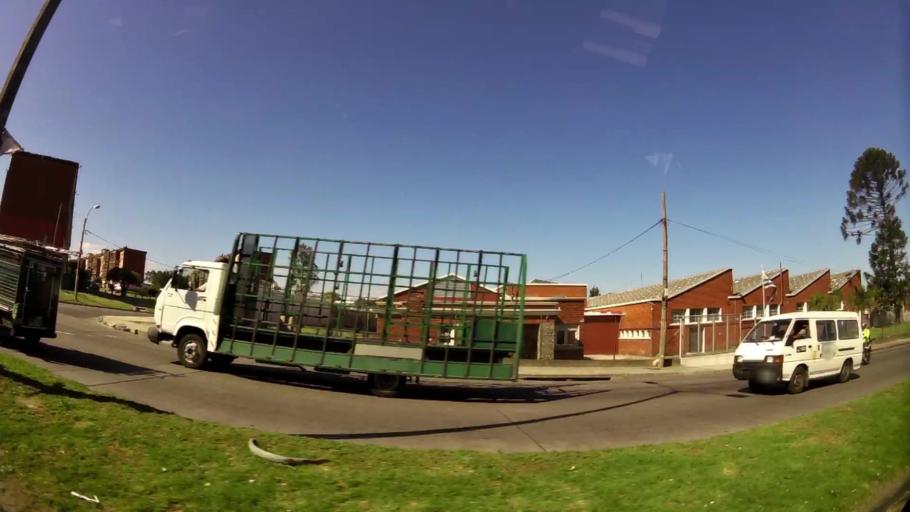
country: UY
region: Montevideo
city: Montevideo
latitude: -34.8426
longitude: -56.1946
